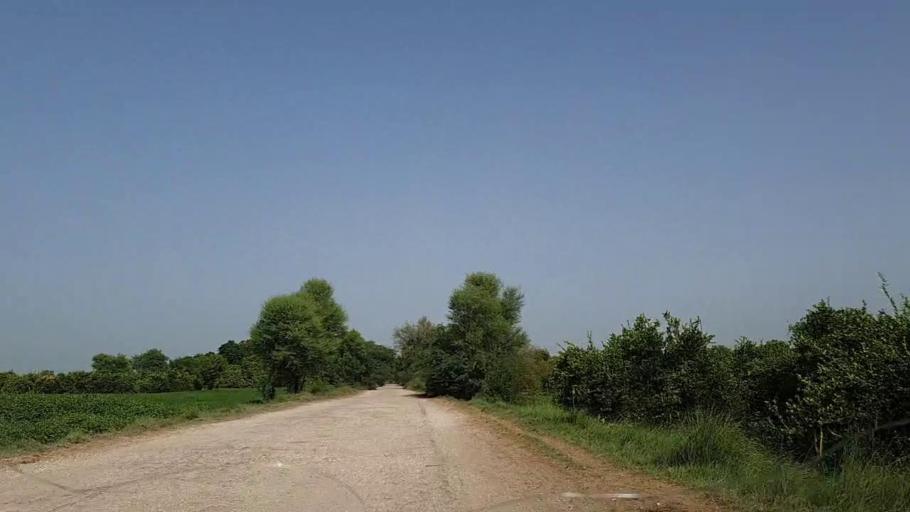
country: PK
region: Sindh
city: Kandiaro
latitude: 27.0658
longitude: 68.1820
